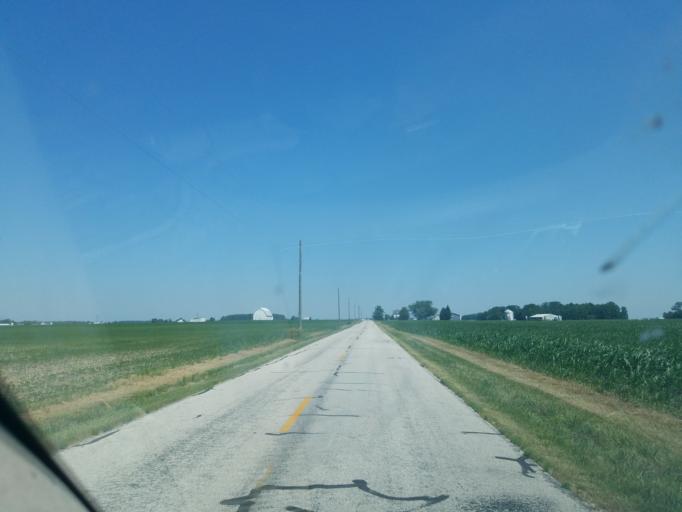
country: US
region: Ohio
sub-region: Mercer County
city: Rockford
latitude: 40.5978
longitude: -84.7084
